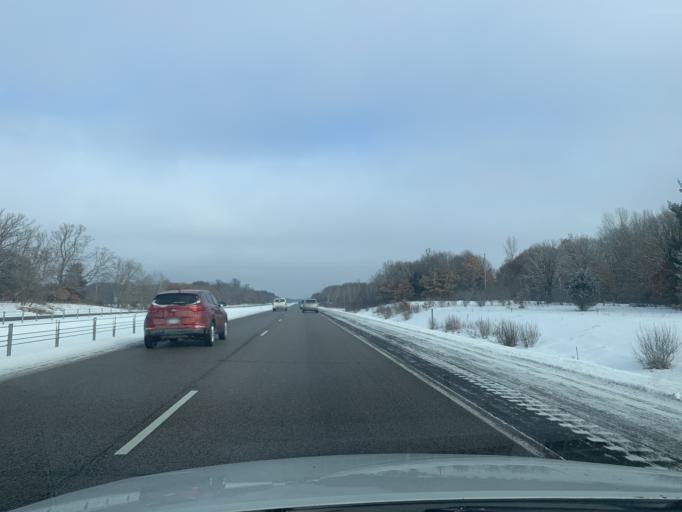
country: US
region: Minnesota
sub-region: Chisago County
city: Wyoming
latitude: 45.3572
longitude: -92.9977
